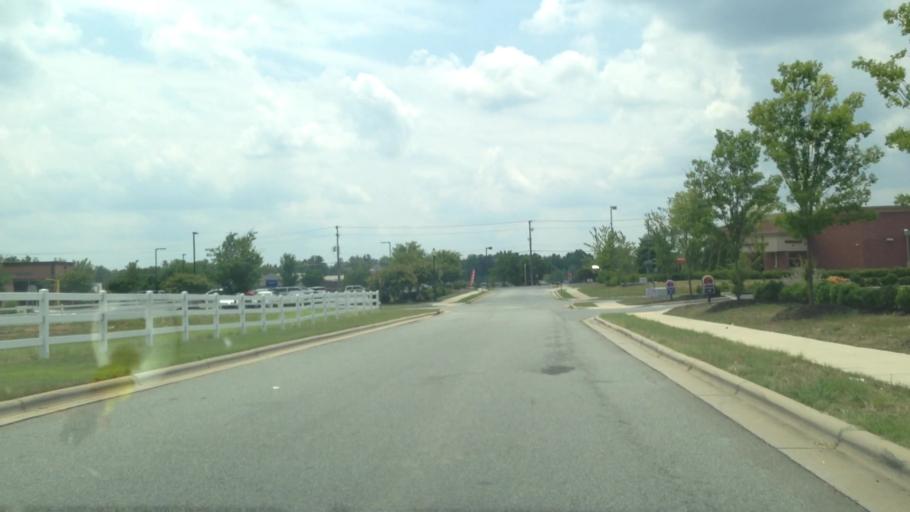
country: US
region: North Carolina
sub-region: Forsyth County
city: Walkertown
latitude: 36.1659
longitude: -80.1348
